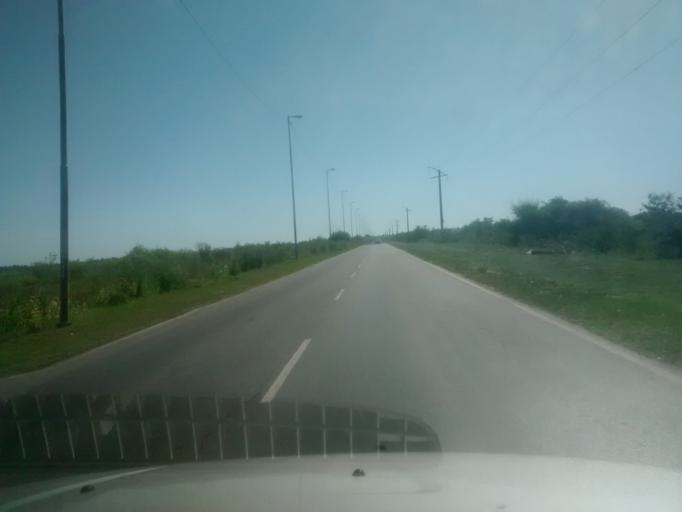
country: AR
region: Buenos Aires
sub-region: Partido de Berisso
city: Berisso
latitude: -34.8945
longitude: -57.8792
